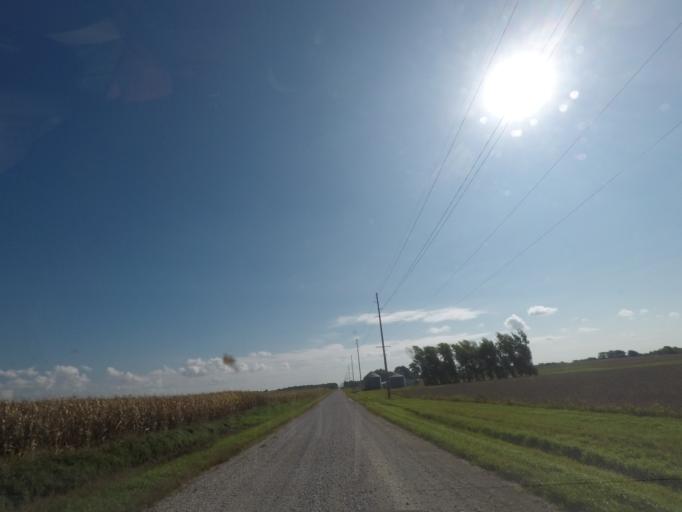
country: US
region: Iowa
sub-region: Story County
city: Nevada
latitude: 42.0343
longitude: -93.3873
